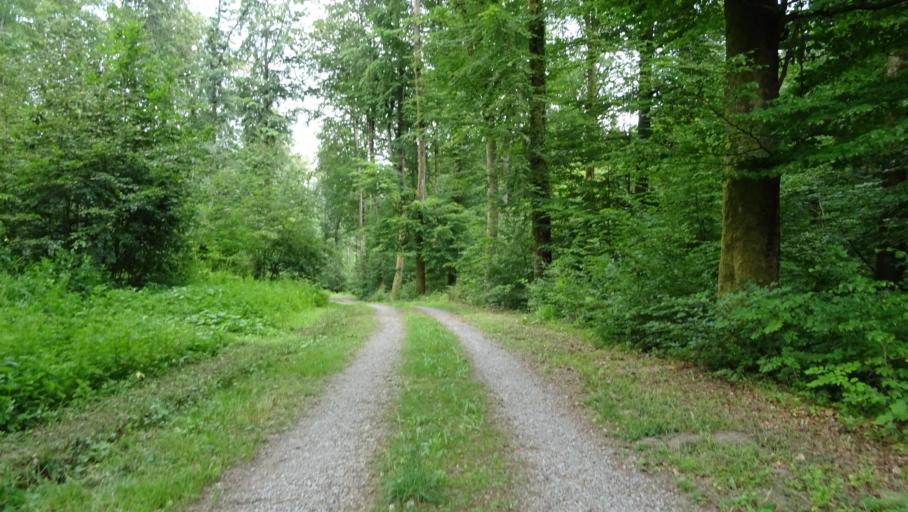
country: DE
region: Baden-Wuerttemberg
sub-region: Karlsruhe Region
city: Obrigheim
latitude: 49.3813
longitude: 9.1127
